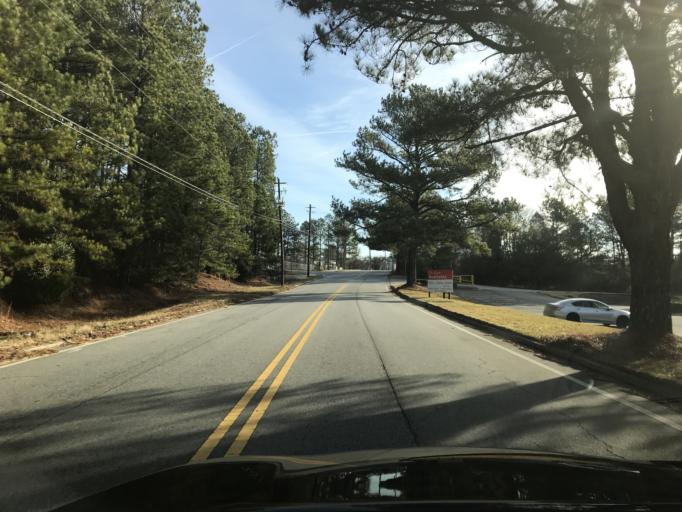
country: US
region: Georgia
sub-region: Clayton County
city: Morrow
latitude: 33.5668
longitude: -84.3481
